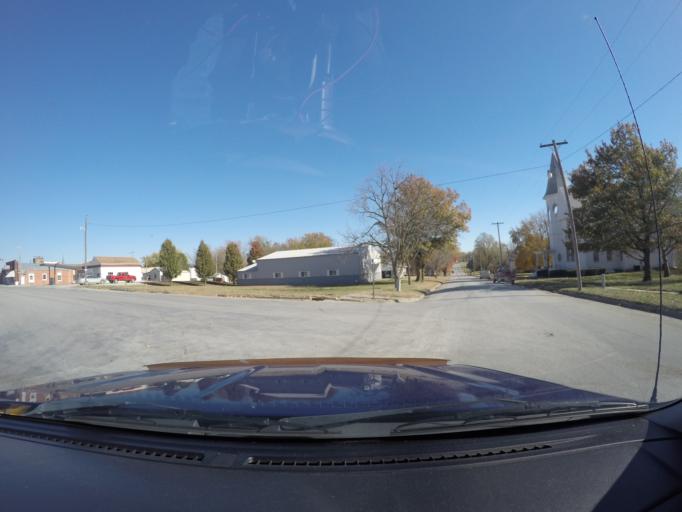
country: US
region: Kansas
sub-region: Nemaha County
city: Seneca
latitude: 39.8709
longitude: -96.2580
